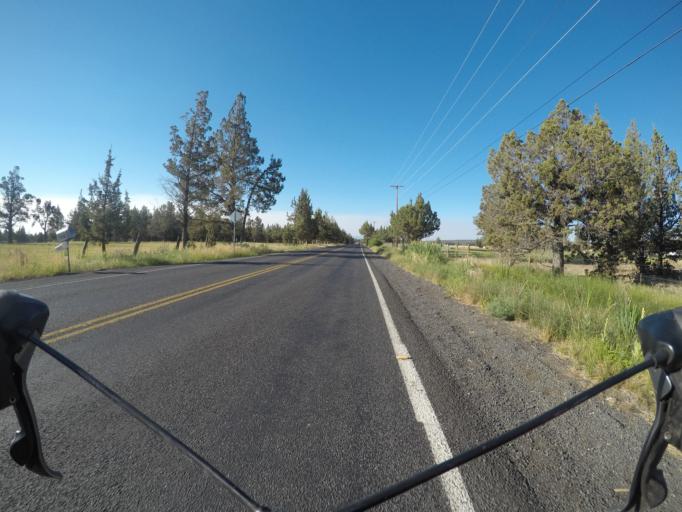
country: US
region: Oregon
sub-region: Deschutes County
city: Redmond
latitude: 44.2088
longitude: -121.2436
